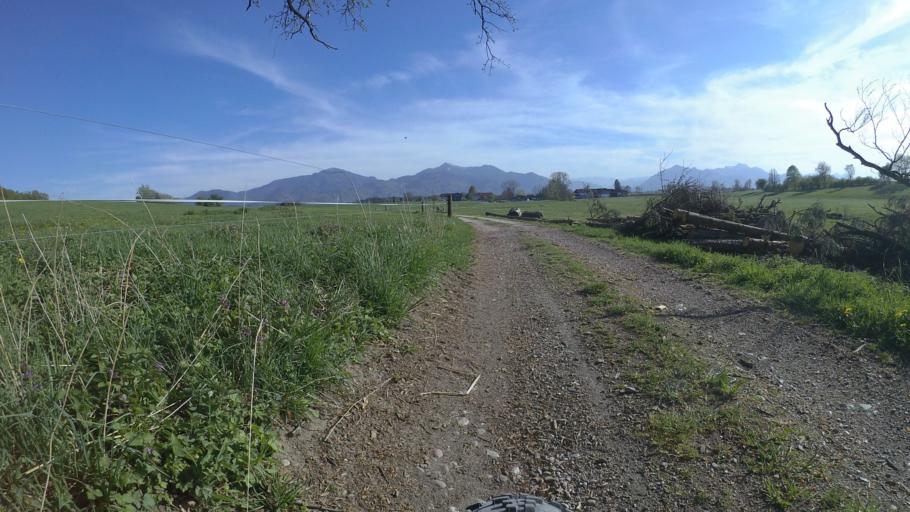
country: DE
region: Bavaria
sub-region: Upper Bavaria
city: Grabenstatt
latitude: 47.8630
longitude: 12.5389
